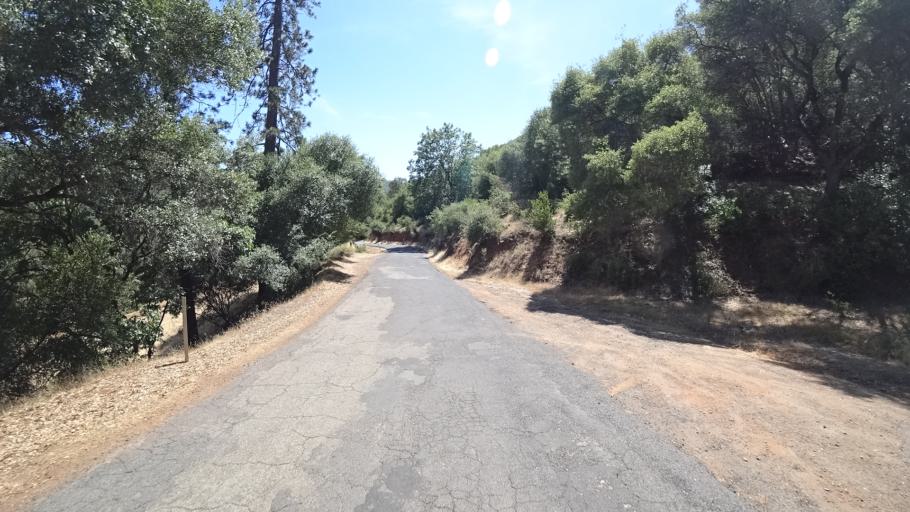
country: US
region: California
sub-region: Calaveras County
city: Murphys
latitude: 38.1656
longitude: -120.4729
